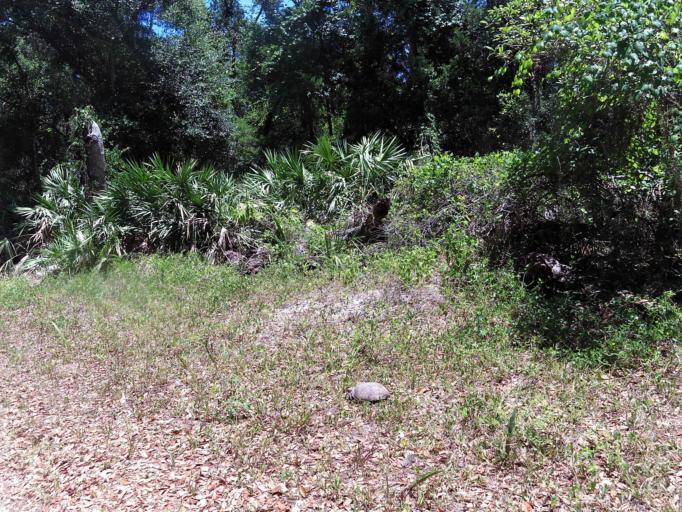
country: US
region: Florida
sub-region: Saint Johns County
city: Villano Beach
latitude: 30.0331
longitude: -81.3378
